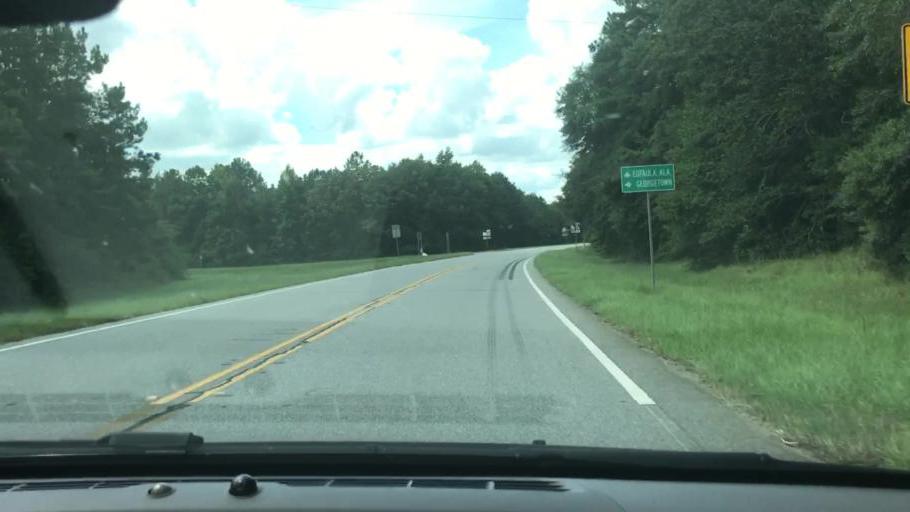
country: US
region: Georgia
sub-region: Stewart County
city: Lumpkin
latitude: 32.1409
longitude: -85.0239
